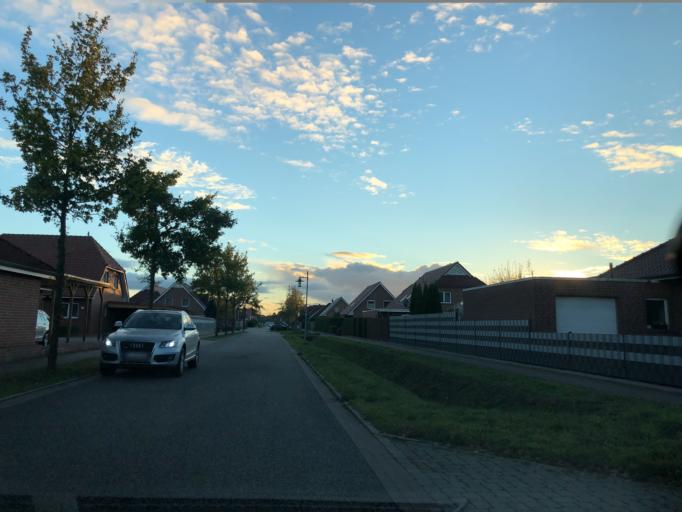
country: DE
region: Lower Saxony
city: Papenburg
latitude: 53.0876
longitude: 7.4213
